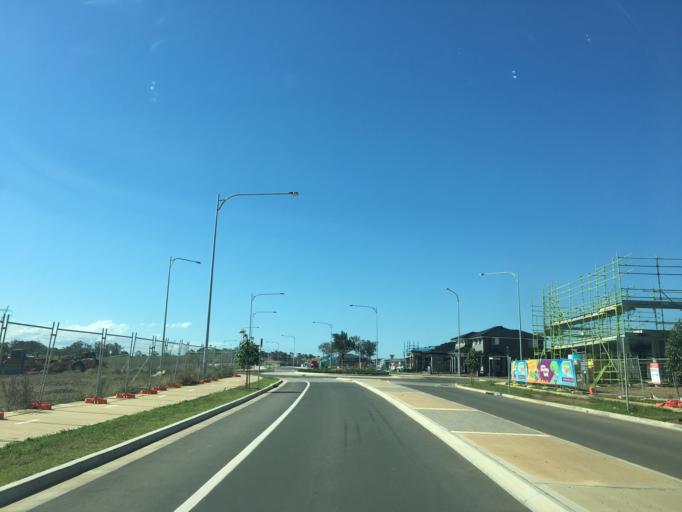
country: AU
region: New South Wales
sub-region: Campbelltown Municipality
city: Denham Court
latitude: -33.9939
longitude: 150.7946
